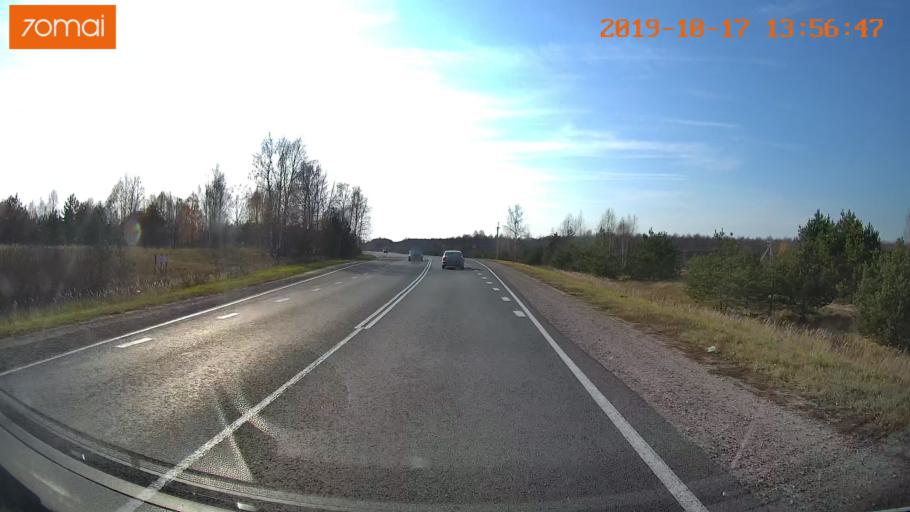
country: RU
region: Rjazan
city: Spas-Klepiki
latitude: 55.1492
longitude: 40.2586
